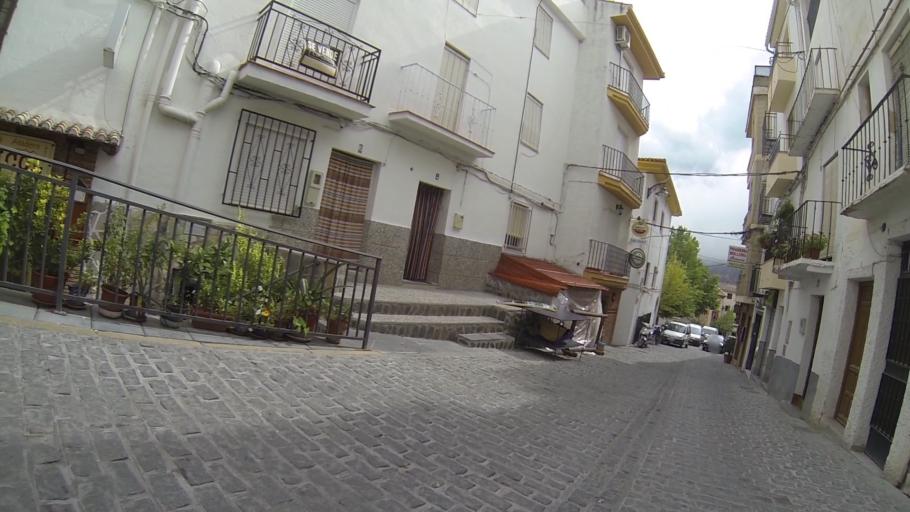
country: ES
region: Andalusia
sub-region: Provincia de Granada
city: Guejar-Sierra
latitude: 37.1602
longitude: -3.4385
